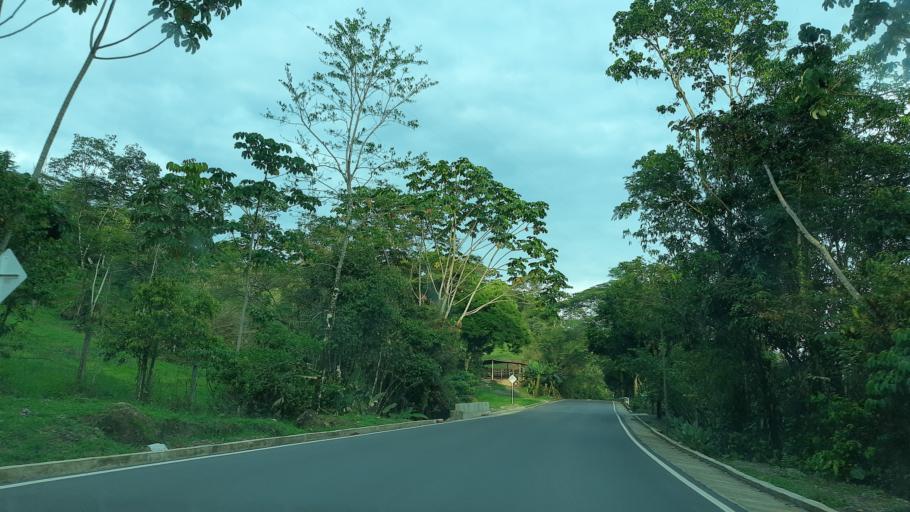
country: CO
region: Boyaca
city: San Luis de Gaceno
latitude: 4.8276
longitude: -73.1061
